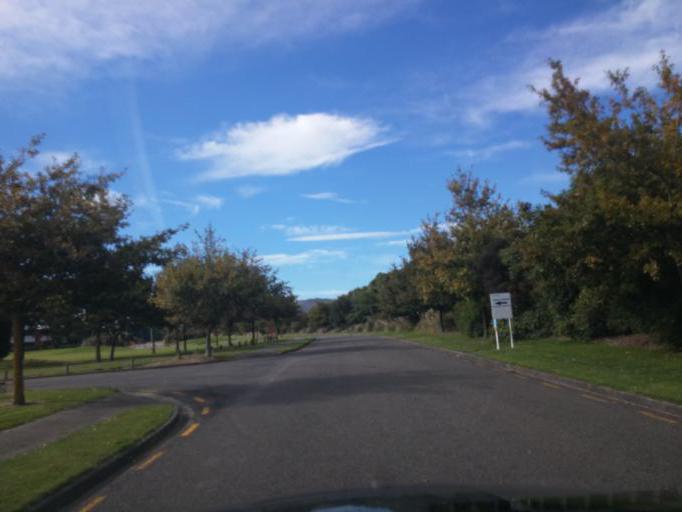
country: NZ
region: Manawatu-Wanganui
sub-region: Palmerston North City
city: Palmerston North
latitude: -40.3916
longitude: 175.6220
